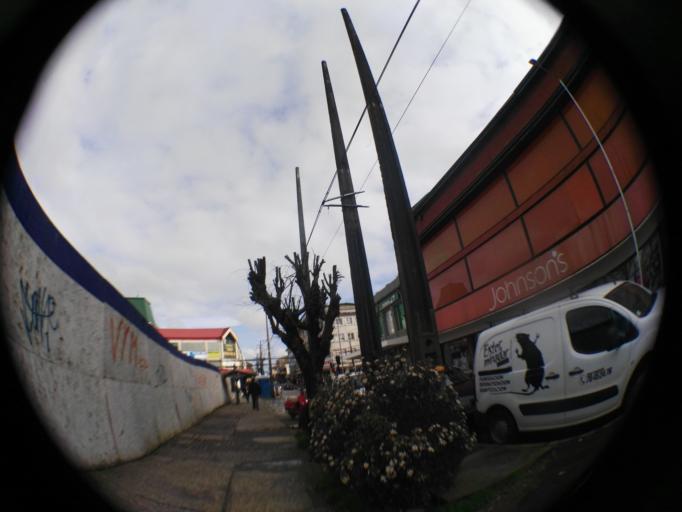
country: CL
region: Los Rios
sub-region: Provincia de Valdivia
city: Valdivia
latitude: -39.8140
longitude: -73.2439
